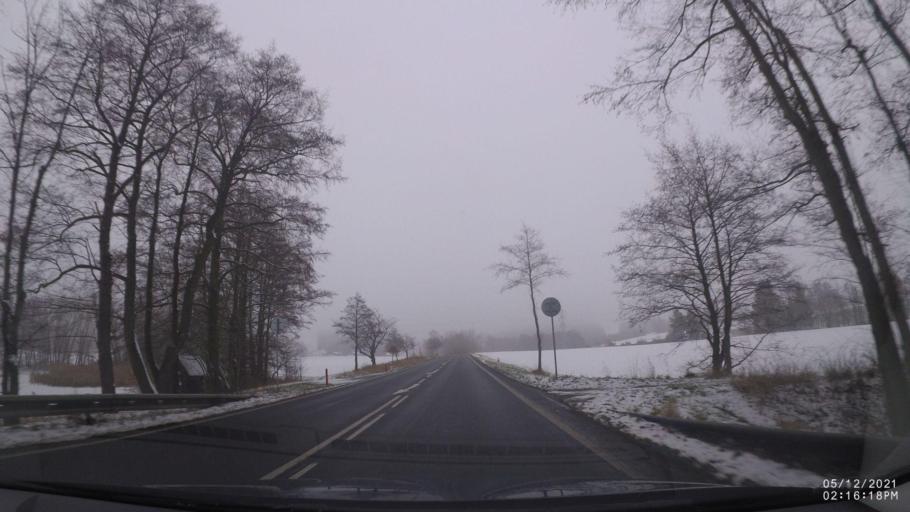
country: CZ
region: Kralovehradecky
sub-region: Okres Nachod
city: Cerveny Kostelec
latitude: 50.4698
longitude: 16.1118
